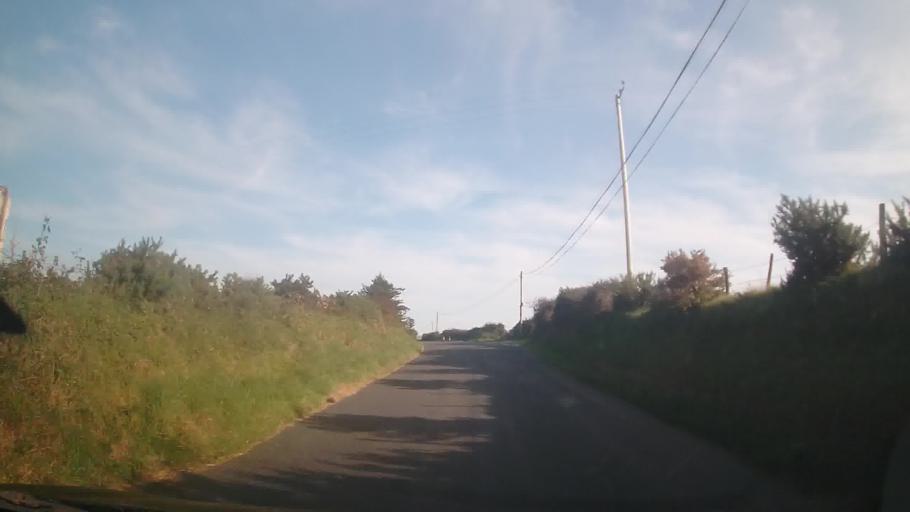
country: GB
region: Wales
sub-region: Pembrokeshire
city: Fishguard
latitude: 51.9896
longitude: -4.9633
